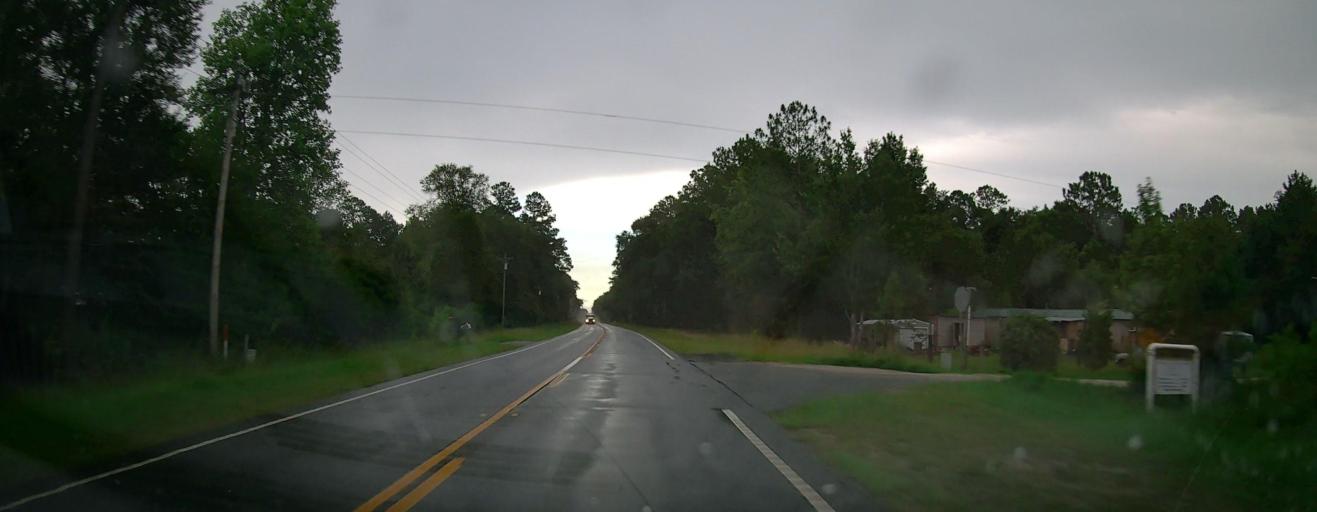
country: US
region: Georgia
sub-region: Glynn County
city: Dock Junction
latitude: 31.3162
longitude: -81.7452
